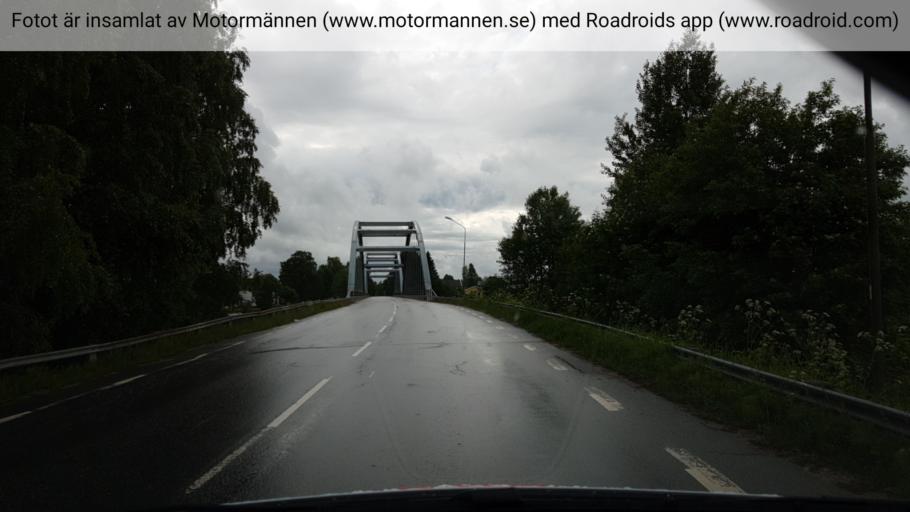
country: SE
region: Vaesterbotten
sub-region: Vannas Kommun
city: Vannasby
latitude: 63.9150
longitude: 19.8431
